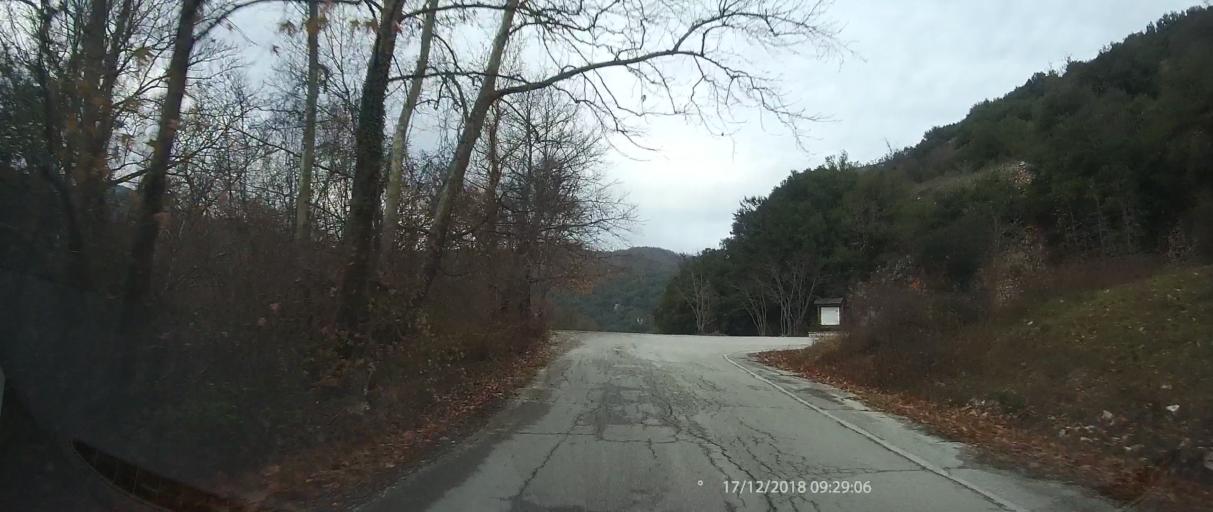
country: GR
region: Epirus
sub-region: Nomos Ioanninon
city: Kalpaki
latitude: 39.9467
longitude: 20.6880
